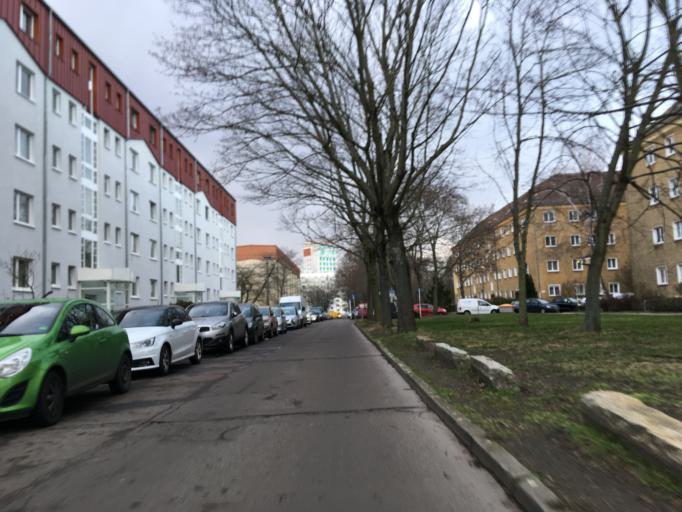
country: DE
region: Berlin
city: Fennpfuhl
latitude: 52.5274
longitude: 13.4641
